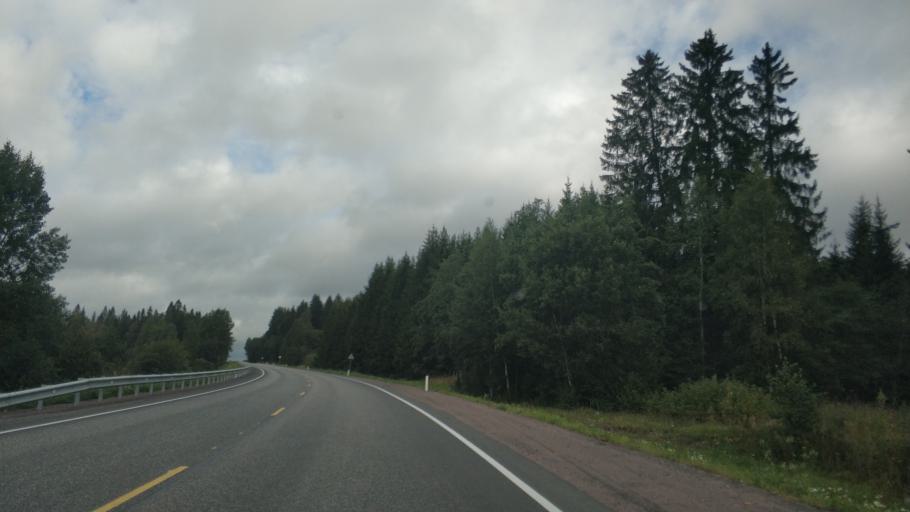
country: RU
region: Republic of Karelia
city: Khelyulya
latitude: 61.7916
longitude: 30.6298
